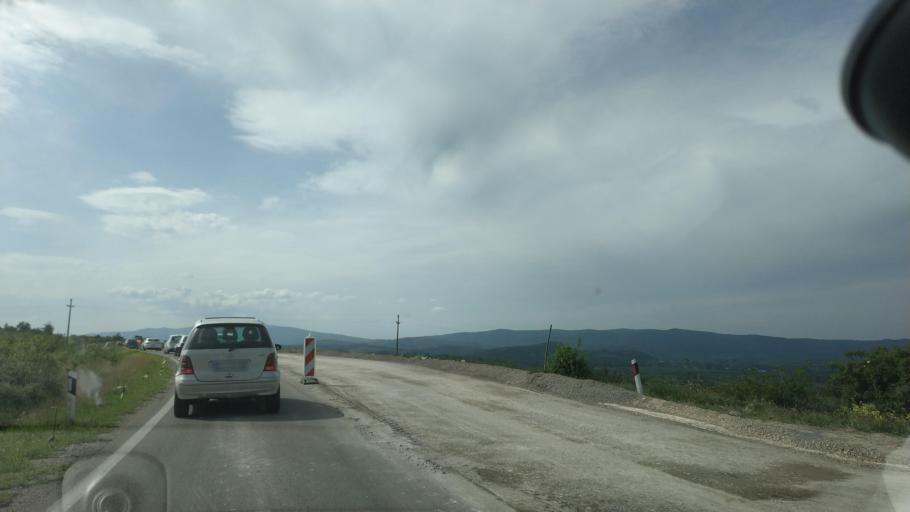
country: RS
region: Central Serbia
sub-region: Nisavski Okrug
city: Merosina
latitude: 43.2738
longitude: 21.7018
